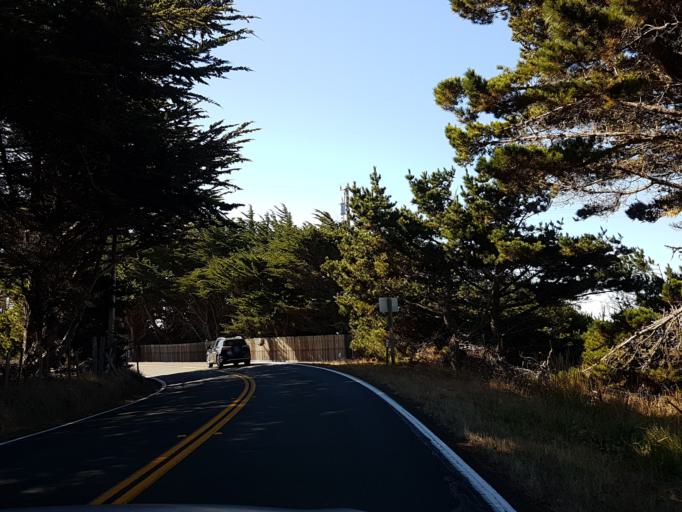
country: US
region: California
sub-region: Mendocino County
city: Boonville
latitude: 39.0190
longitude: -123.6881
